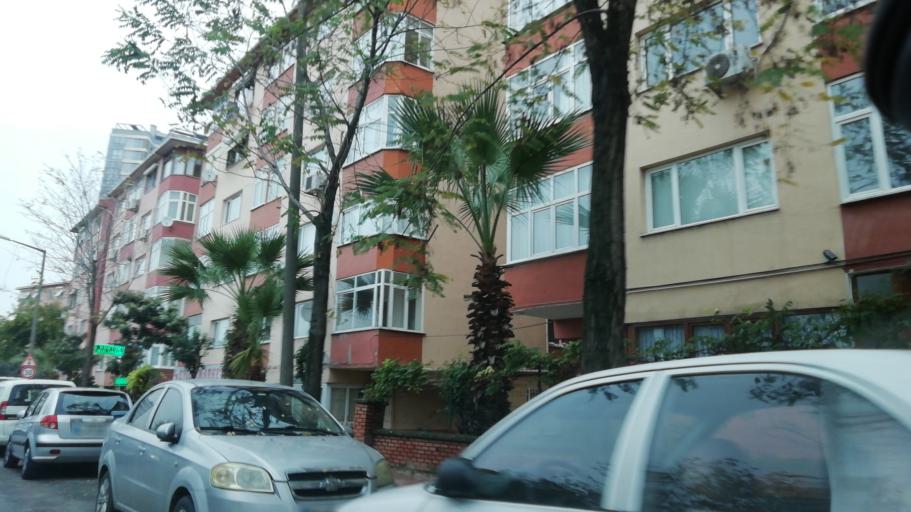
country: TR
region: Istanbul
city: Mahmutbey
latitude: 41.0187
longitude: 28.8223
